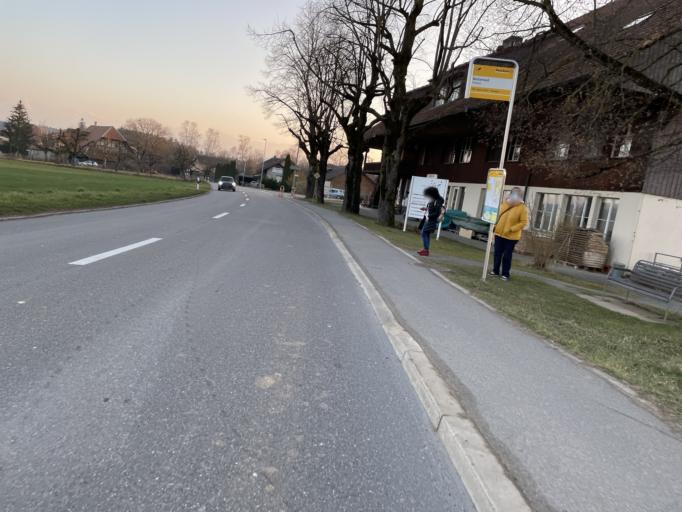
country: CH
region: Bern
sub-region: Bern-Mittelland District
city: Rubigen
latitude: 46.9101
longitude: 7.5583
